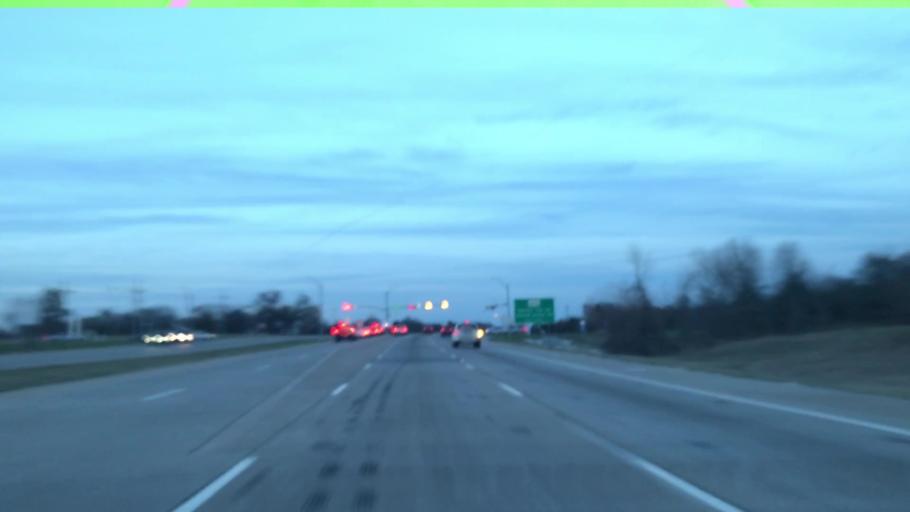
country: US
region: Texas
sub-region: Dallas County
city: Coppell
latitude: 32.9936
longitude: -97.0051
